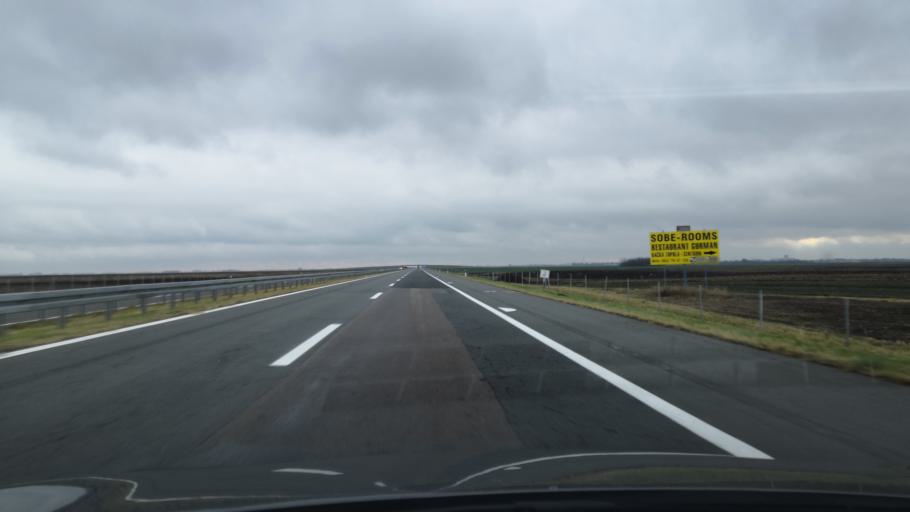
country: RS
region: Autonomna Pokrajina Vojvodina
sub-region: Severnobacki Okrug
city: Backa Topola
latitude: 45.8514
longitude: 19.6958
